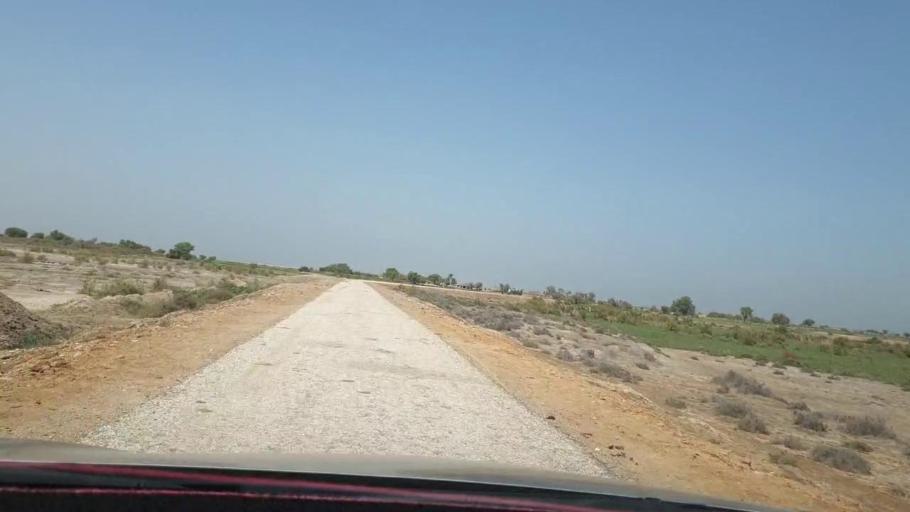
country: PK
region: Sindh
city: Warah
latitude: 27.5217
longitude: 67.7086
